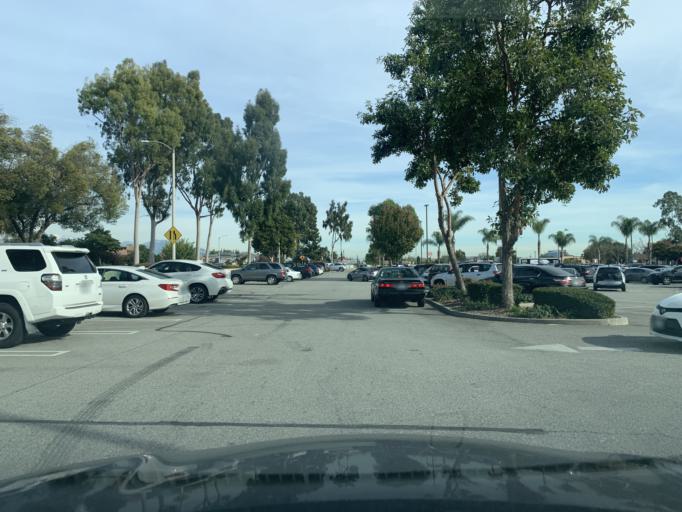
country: US
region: California
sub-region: Los Angeles County
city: Rosemead
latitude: 34.0754
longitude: -118.0710
